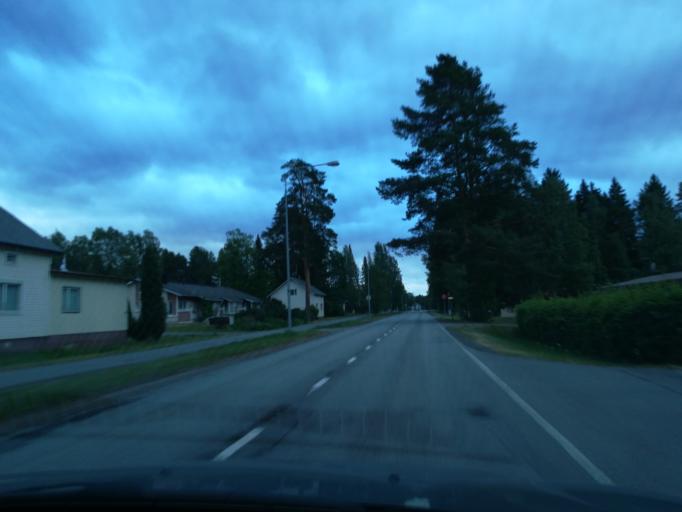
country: FI
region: Southern Savonia
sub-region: Mikkeli
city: Ristiina
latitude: 61.5092
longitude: 27.2511
